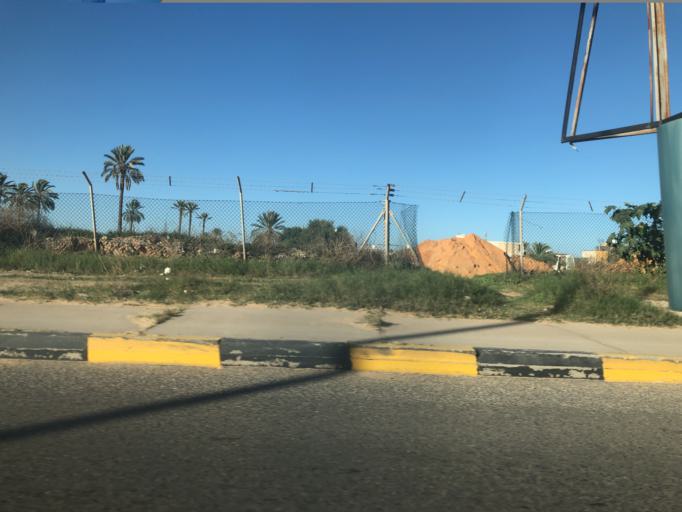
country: LY
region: Tripoli
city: Tripoli
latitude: 32.8701
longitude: 13.2678
